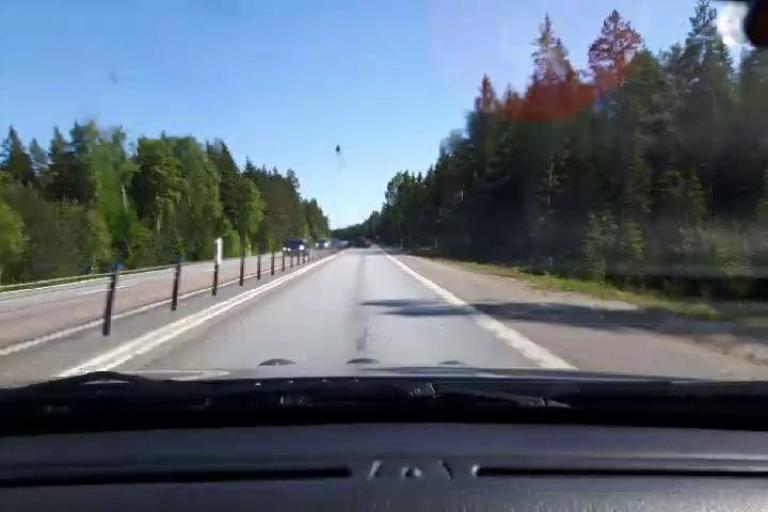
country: SE
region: Gaevleborg
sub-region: Gavle Kommun
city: Norrsundet
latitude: 60.8622
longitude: 17.0606
